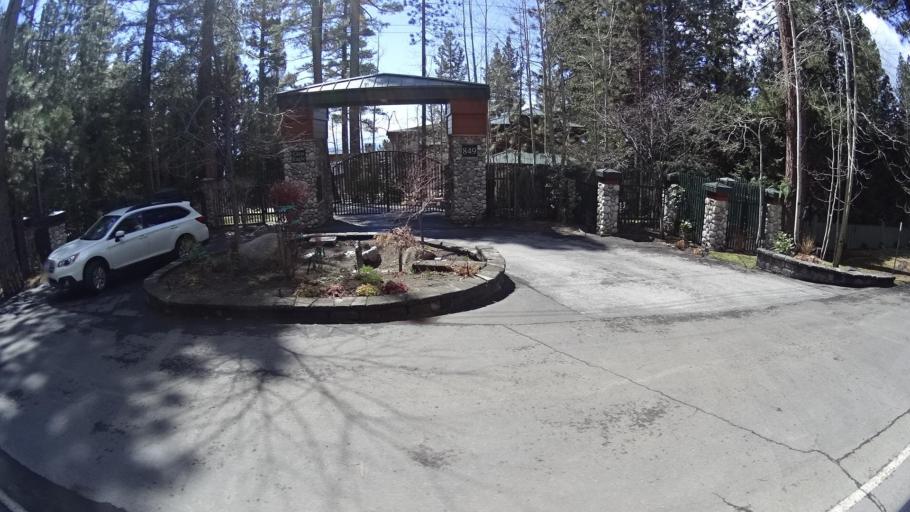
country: US
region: Nevada
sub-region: Washoe County
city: Incline Village
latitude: 39.2438
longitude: -119.9592
